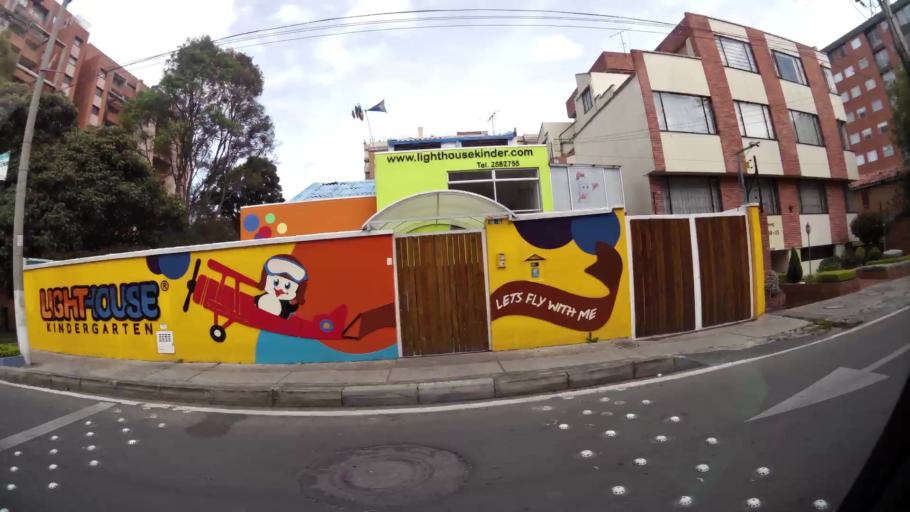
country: CO
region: Bogota D.C.
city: Barrio San Luis
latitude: 4.7157
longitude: -74.0307
